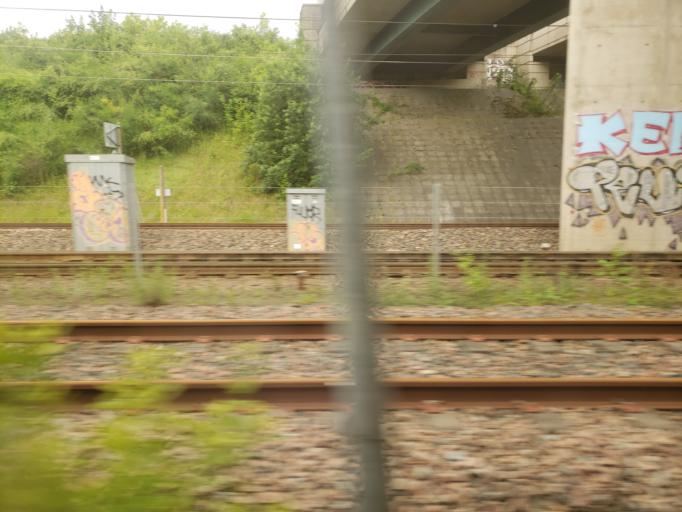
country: FR
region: Ile-de-France
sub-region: Departement de Seine-et-Marne
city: Serris
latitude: 48.8622
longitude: 2.7812
